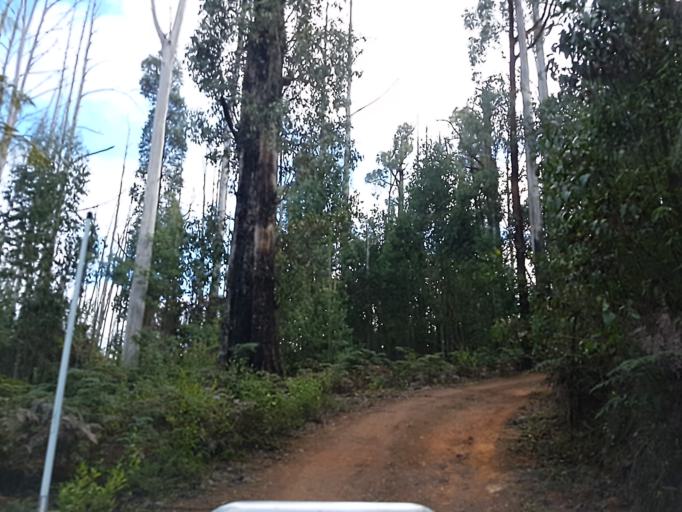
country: AU
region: Victoria
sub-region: Yarra Ranges
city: Millgrove
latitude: -37.5408
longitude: 145.7386
